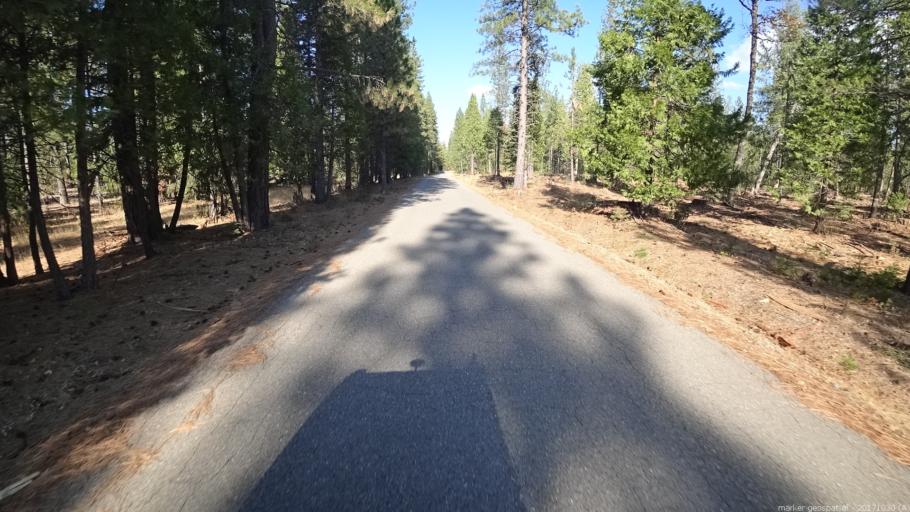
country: US
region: California
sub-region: Shasta County
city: Shingletown
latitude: 40.5151
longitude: -121.7248
